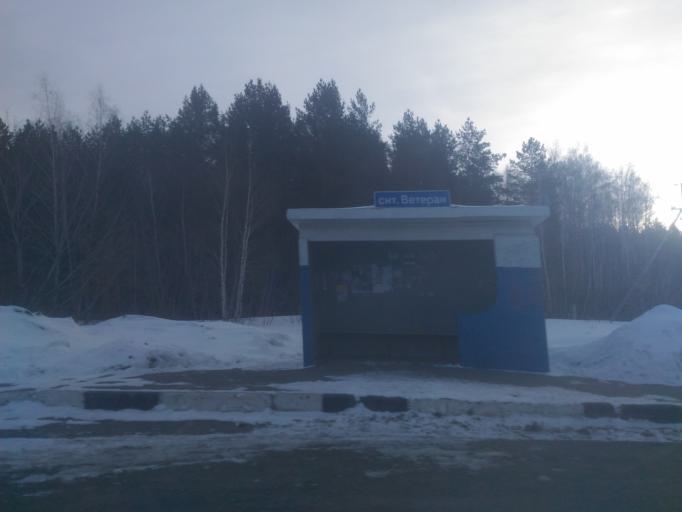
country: RU
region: Ulyanovsk
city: Isheyevka
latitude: 54.3764
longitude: 48.3089
